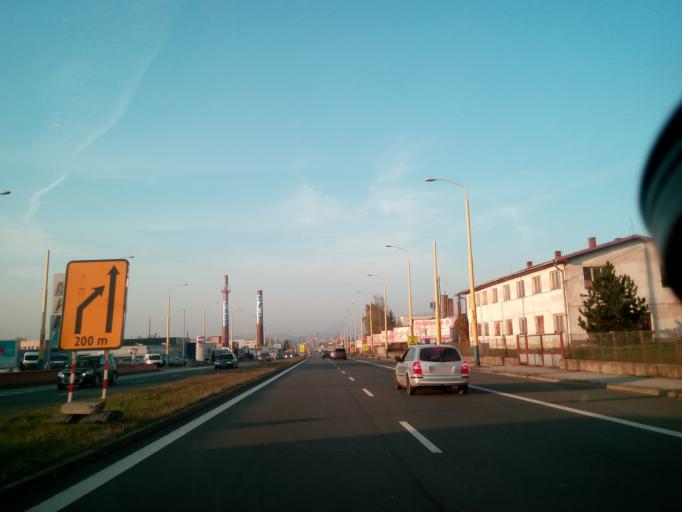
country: SK
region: Presovsky
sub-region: Okres Presov
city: Presov
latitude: 48.9641
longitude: 21.2553
